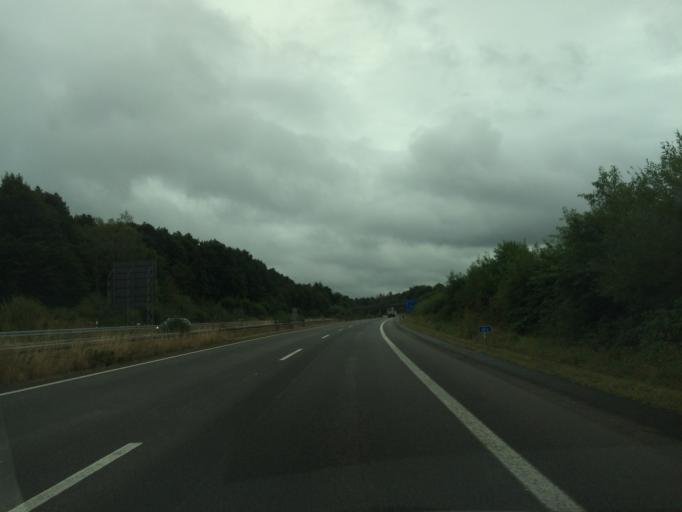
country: DE
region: Saarland
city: Saarwellingen
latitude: 49.3381
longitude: 6.8029
